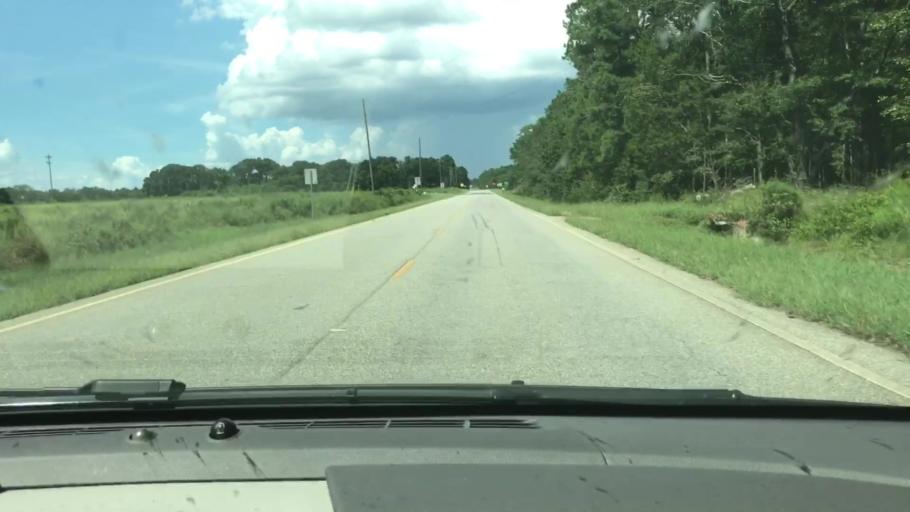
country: US
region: Georgia
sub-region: Quitman County
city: Georgetown
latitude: 31.7775
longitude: -85.0918
